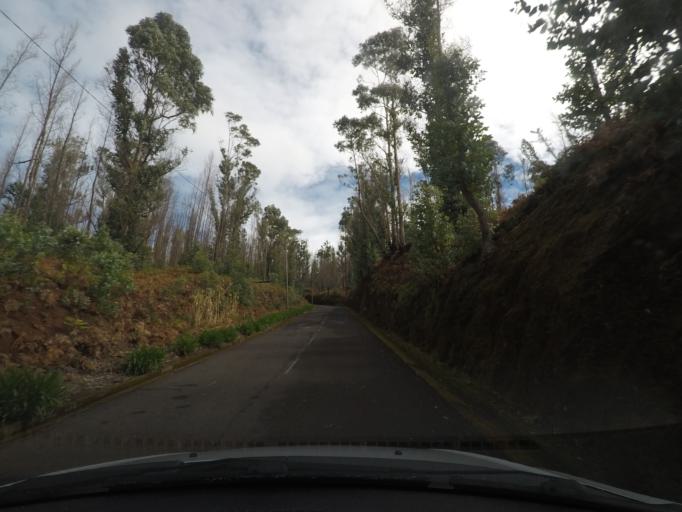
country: PT
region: Madeira
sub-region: Calheta
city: Faja da Ovelha
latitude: 32.8299
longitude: -17.2285
